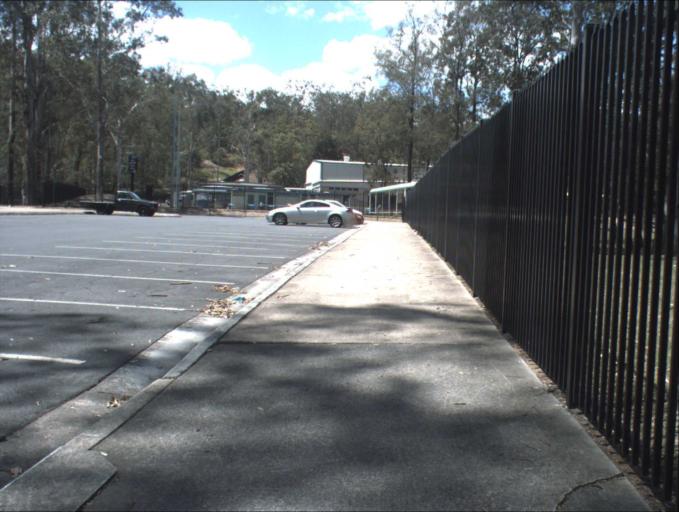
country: AU
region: Queensland
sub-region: Logan
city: Logan City
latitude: -27.6651
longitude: 153.1084
